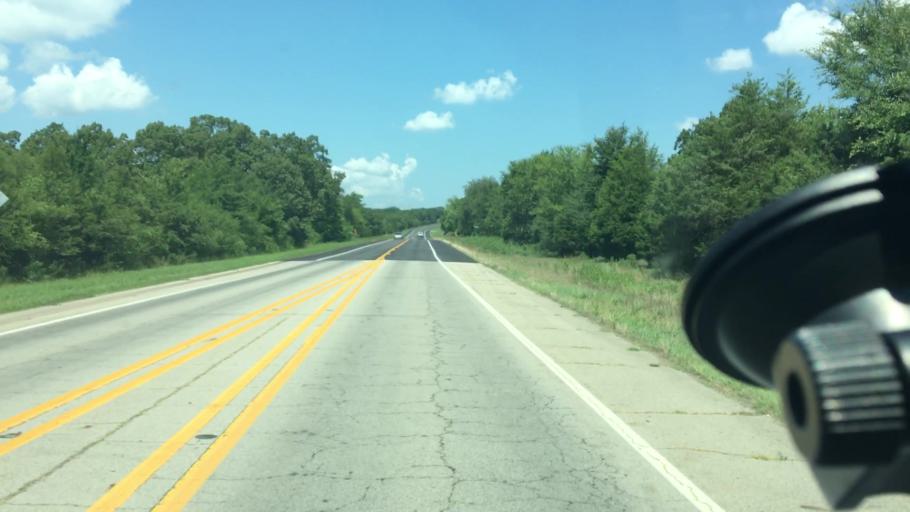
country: US
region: Arkansas
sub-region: Sebastian County
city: Lavaca
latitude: 35.2971
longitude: -94.1501
